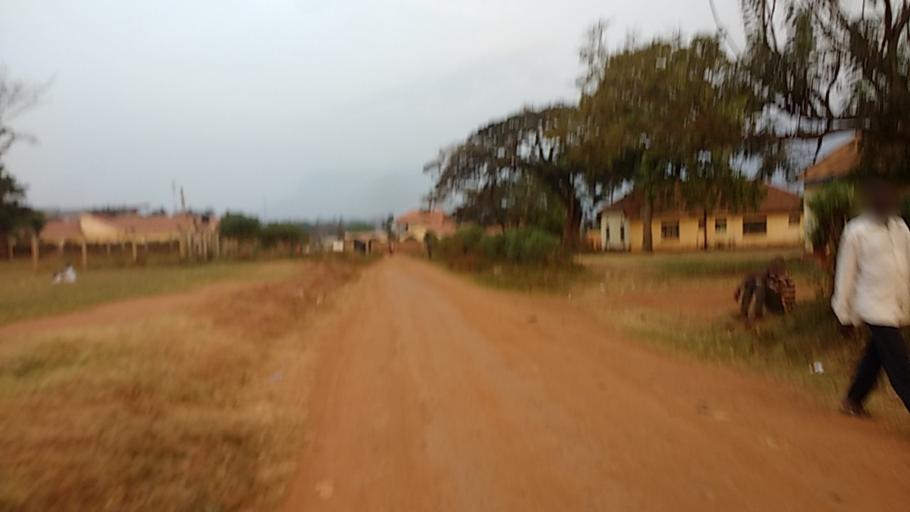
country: UG
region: Eastern Region
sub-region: Mbale District
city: Mbale
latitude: 1.0683
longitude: 34.1688
